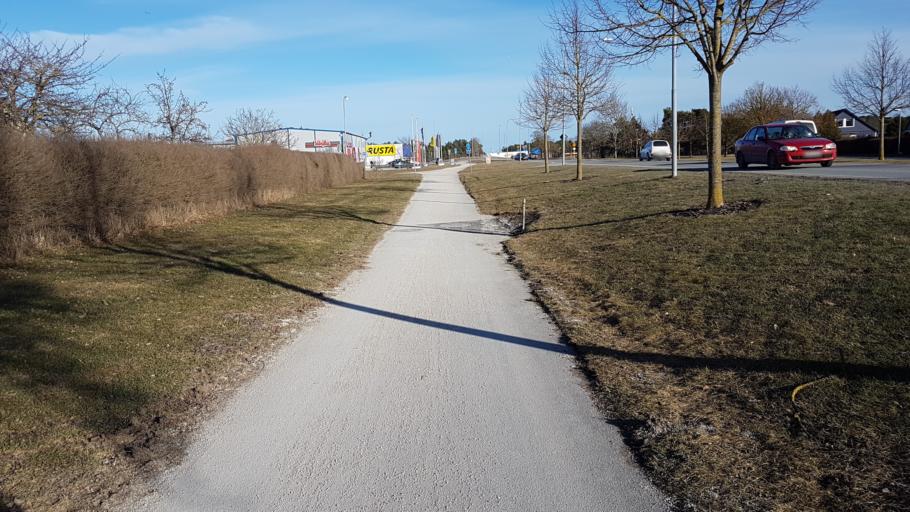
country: SE
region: Gotland
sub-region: Gotland
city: Visby
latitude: 57.6335
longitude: 18.3221
